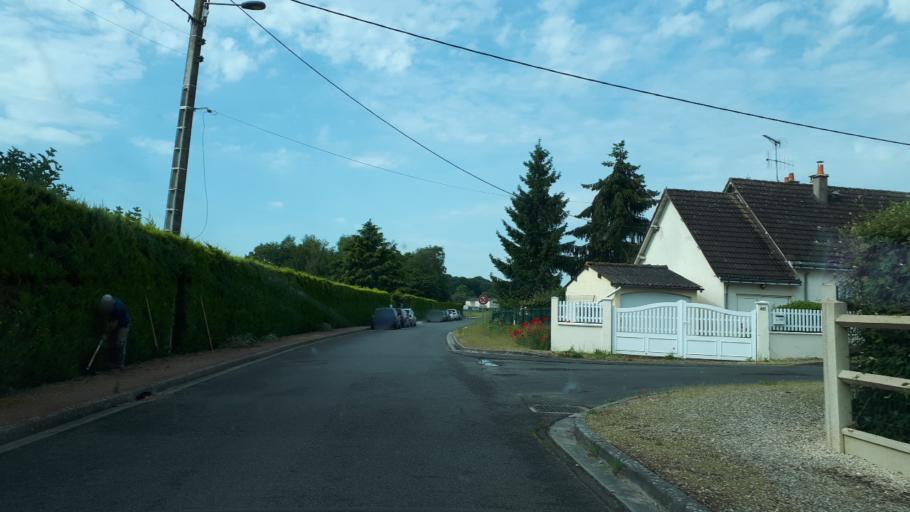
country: FR
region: Centre
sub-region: Departement d'Indre-et-Loire
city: Monnaie
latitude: 47.4972
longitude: 0.7779
